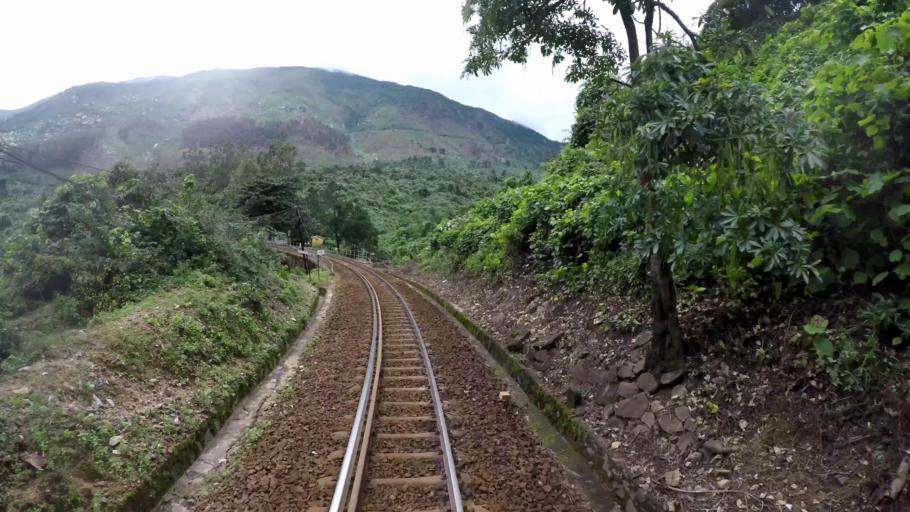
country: VN
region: Da Nang
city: Lien Chieu
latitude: 16.1727
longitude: 108.1378
